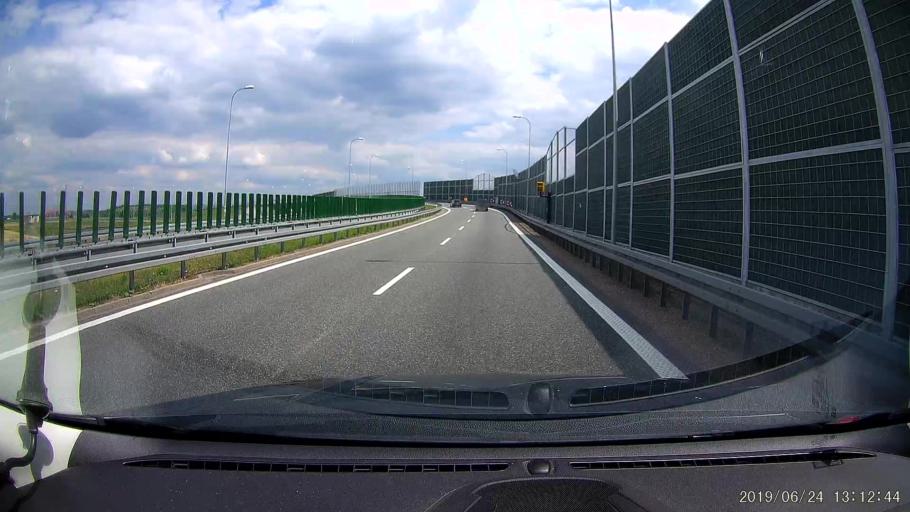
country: PL
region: Silesian Voivodeship
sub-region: Powiat gliwicki
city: Przyszowice
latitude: 50.2585
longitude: 18.7234
